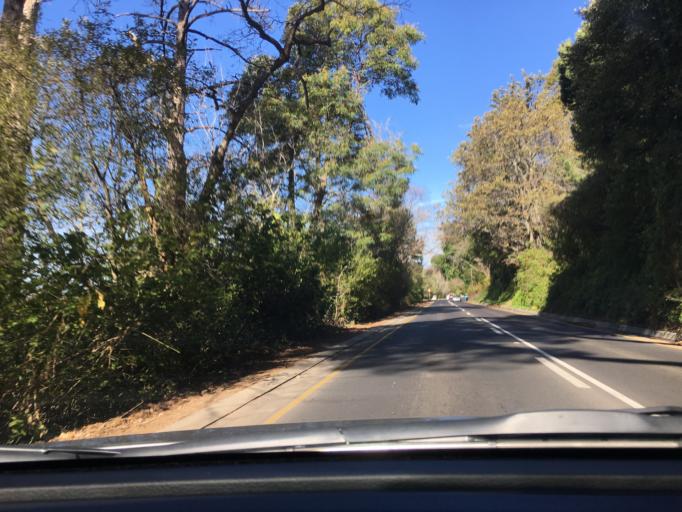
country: ZA
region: Western Cape
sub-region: City of Cape Town
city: Constantia
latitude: -34.0183
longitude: 18.4182
